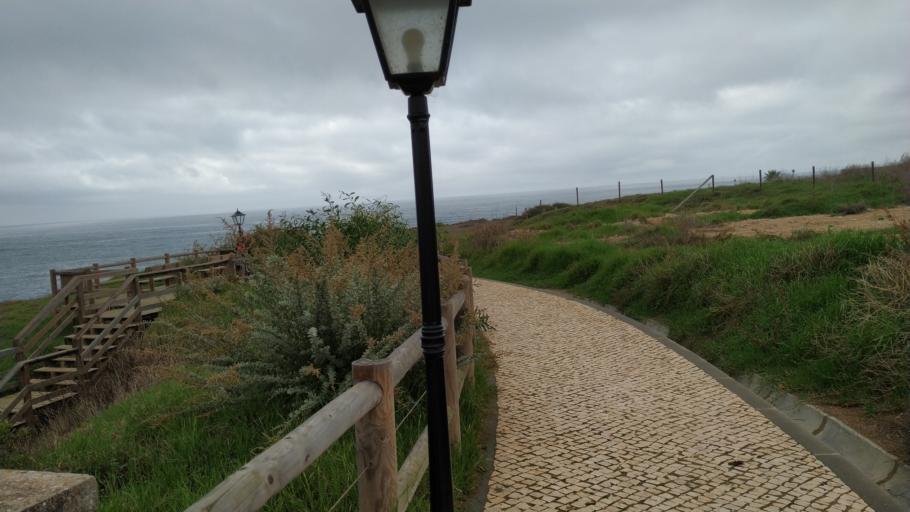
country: PT
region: Setubal
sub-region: Sines
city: Porto Covo
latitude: 37.8498
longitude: -8.7936
